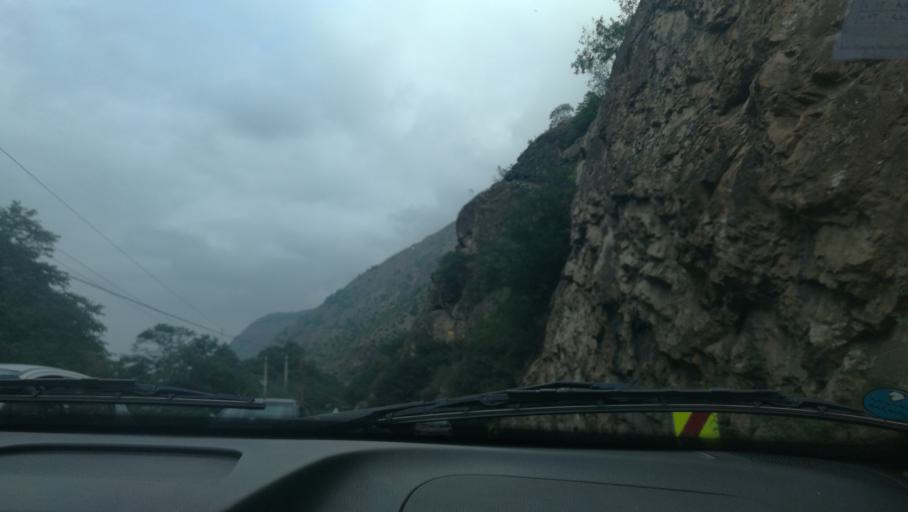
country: IR
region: Mazandaran
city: Chalus
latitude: 36.3226
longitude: 51.2529
